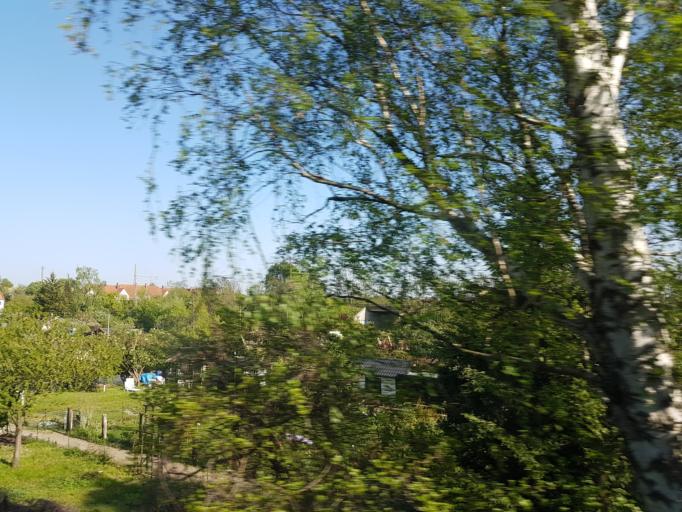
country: DE
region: Lower Saxony
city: Laatzen
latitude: 52.3466
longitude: 9.7717
